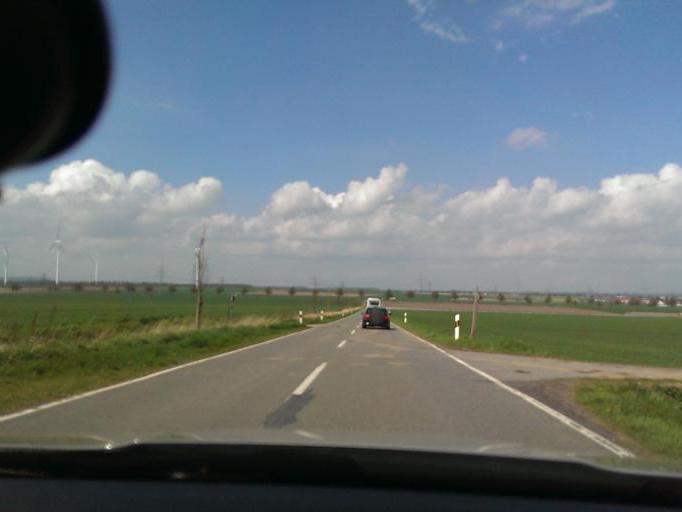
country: DE
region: Lower Saxony
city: Nordstemmen
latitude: 52.1804
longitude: 9.7642
